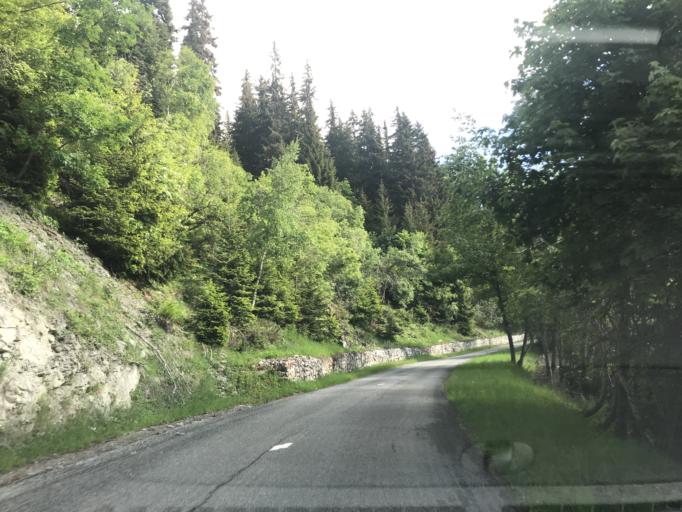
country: FR
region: Rhone-Alpes
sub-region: Departement de la Savoie
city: Modane
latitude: 45.2149
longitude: 6.6484
